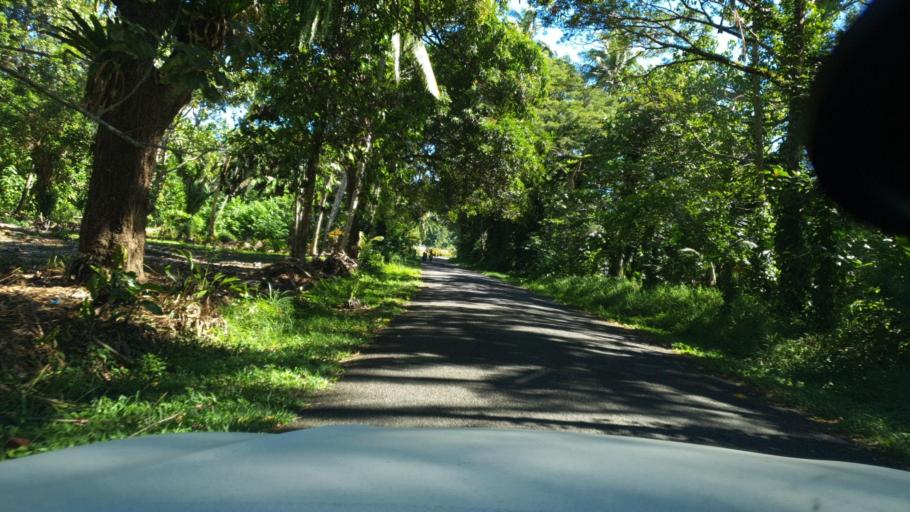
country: SB
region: Guadalcanal
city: Honiara
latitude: -9.2777
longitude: 159.7379
